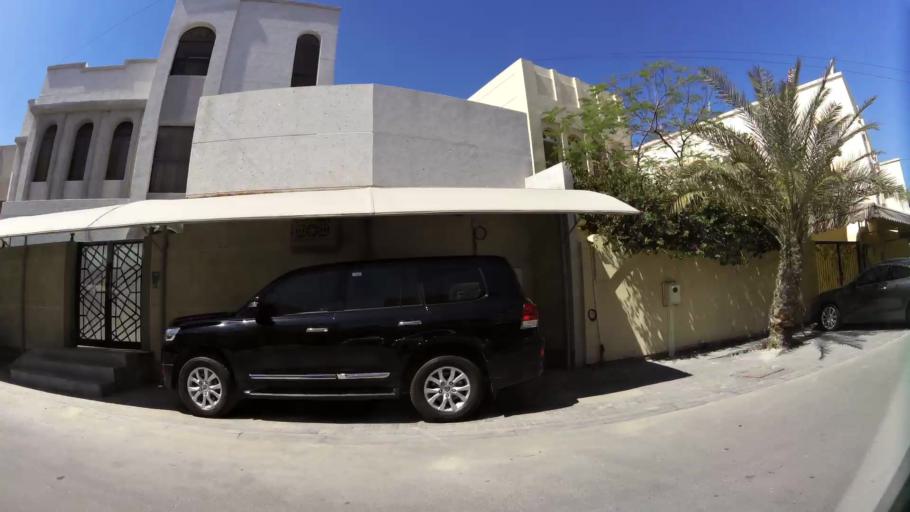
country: BH
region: Muharraq
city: Al Muharraq
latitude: 26.2708
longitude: 50.6064
